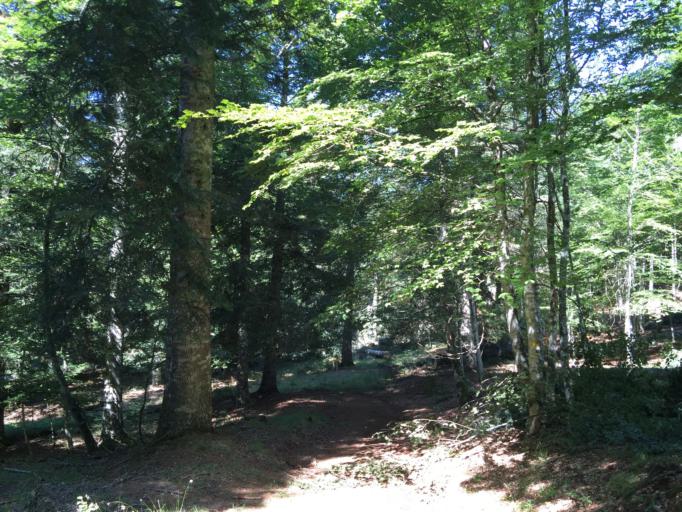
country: FR
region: Midi-Pyrenees
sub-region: Departement de l'Aveyron
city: Laguiole
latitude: 44.6448
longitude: 2.9275
